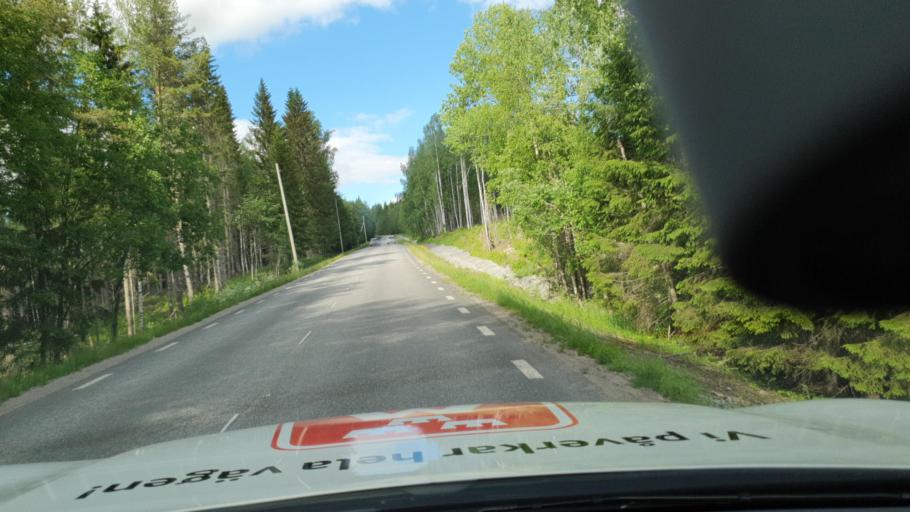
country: SE
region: Vaesterbotten
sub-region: Vannas Kommun
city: Vannasby
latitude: 63.8389
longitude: 19.8613
